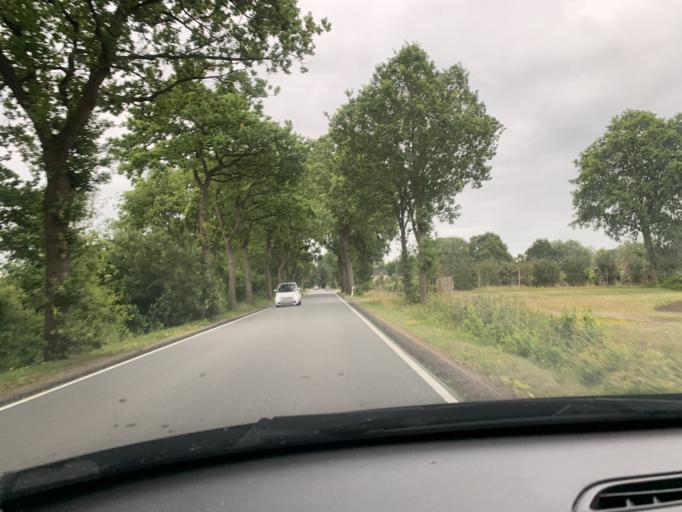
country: DE
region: Lower Saxony
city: Westerstede
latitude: 53.2548
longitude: 7.9602
